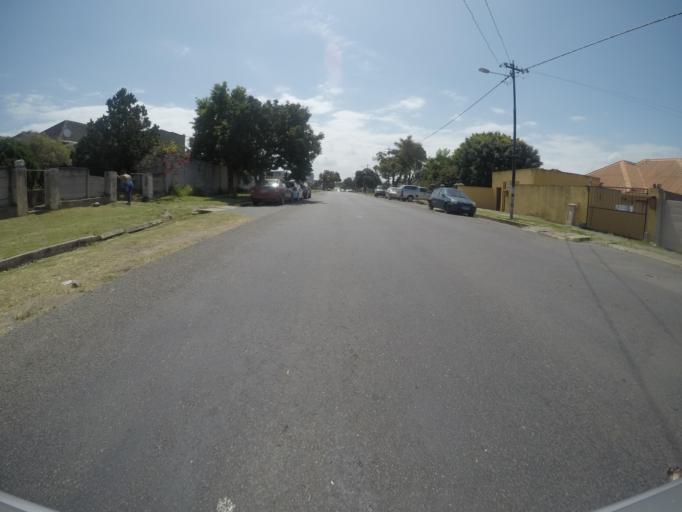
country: ZA
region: Eastern Cape
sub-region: Buffalo City Metropolitan Municipality
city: East London
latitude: -32.9778
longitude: 27.8754
